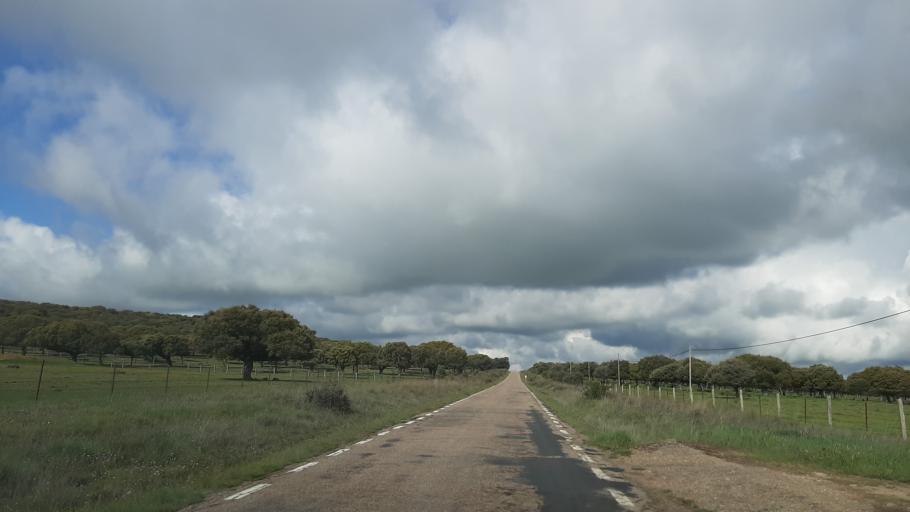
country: ES
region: Castille and Leon
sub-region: Provincia de Salamanca
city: Narros de Matalayegua
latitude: 40.7042
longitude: -5.8976
